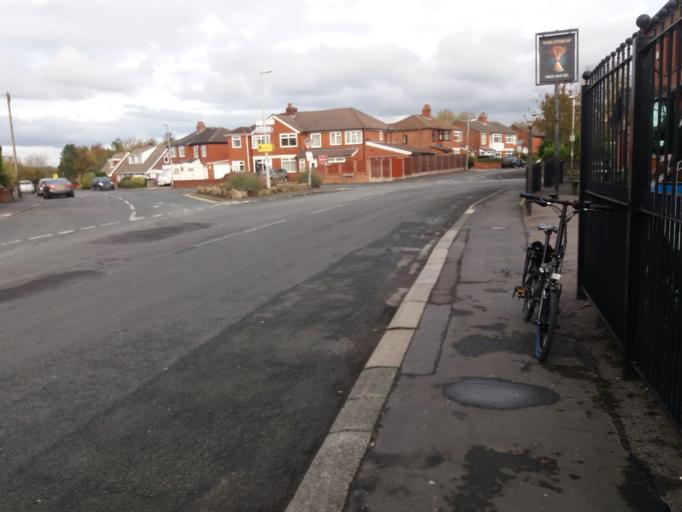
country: GB
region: England
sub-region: Lancashire
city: Coppull
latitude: 53.6277
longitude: -2.6544
